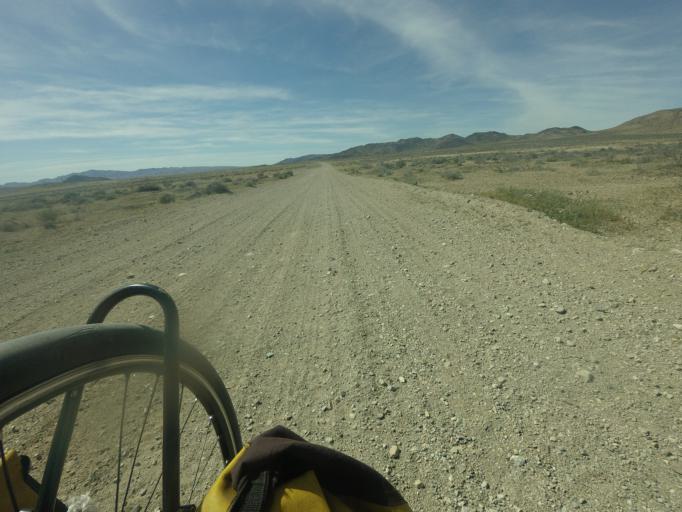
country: US
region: California
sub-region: San Bernardino County
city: Searles Valley
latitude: 35.5949
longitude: -117.4071
